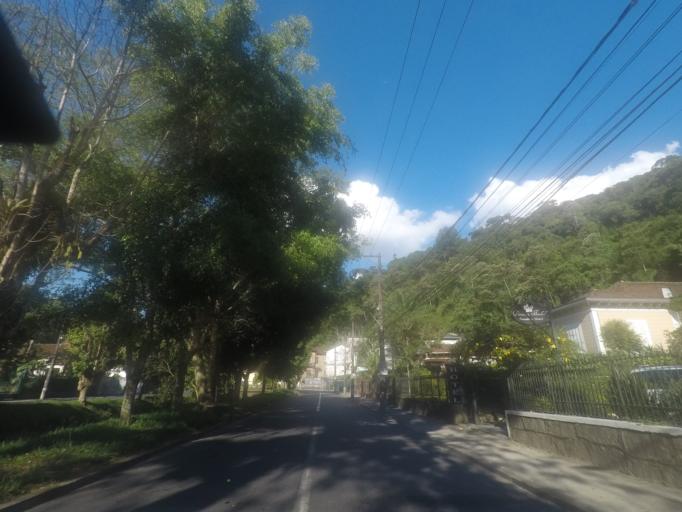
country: BR
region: Rio de Janeiro
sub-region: Petropolis
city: Petropolis
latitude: -22.5124
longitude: -43.1717
